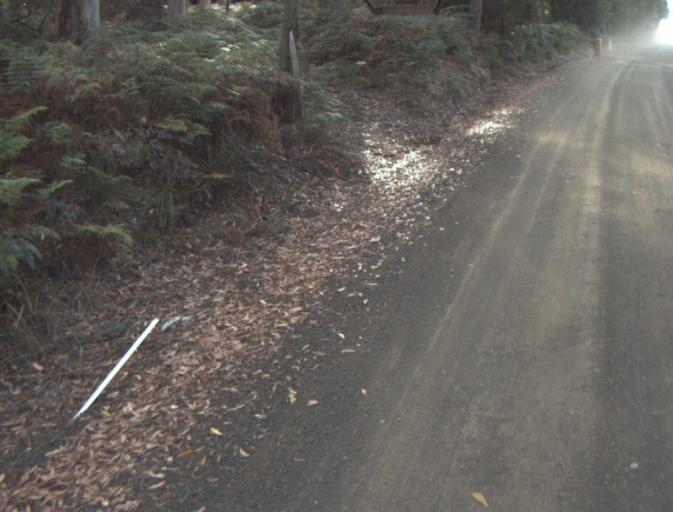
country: AU
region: Tasmania
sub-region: Launceston
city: Mayfield
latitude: -41.2714
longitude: 147.1714
